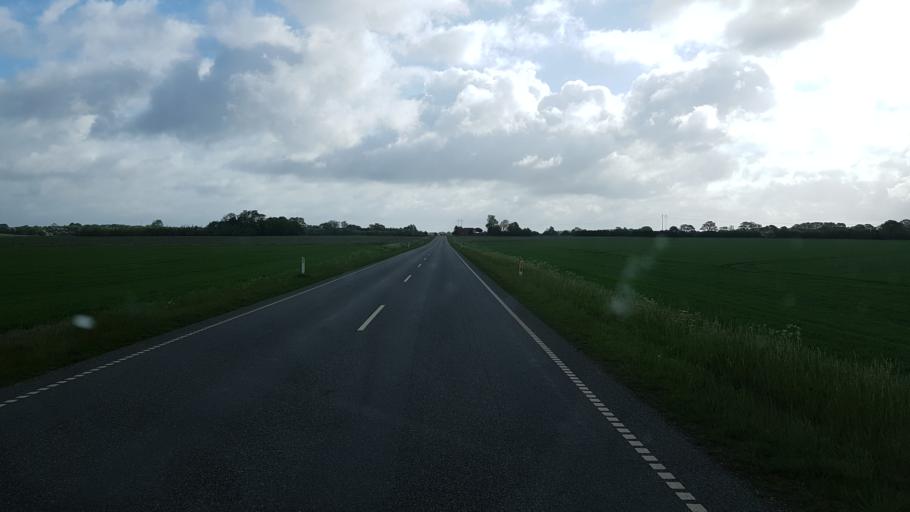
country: DK
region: South Denmark
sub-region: Vejen Kommune
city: Rodding
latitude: 55.4019
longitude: 9.1135
